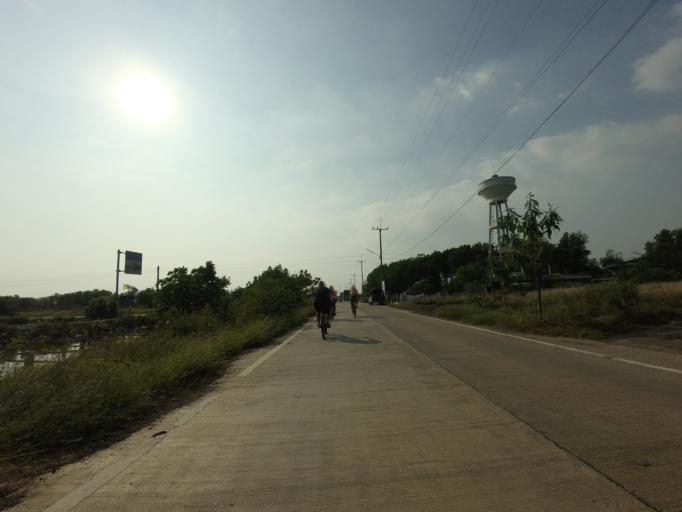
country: TH
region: Samut Sakhon
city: Samut Sakhon
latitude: 13.4982
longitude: 100.3356
